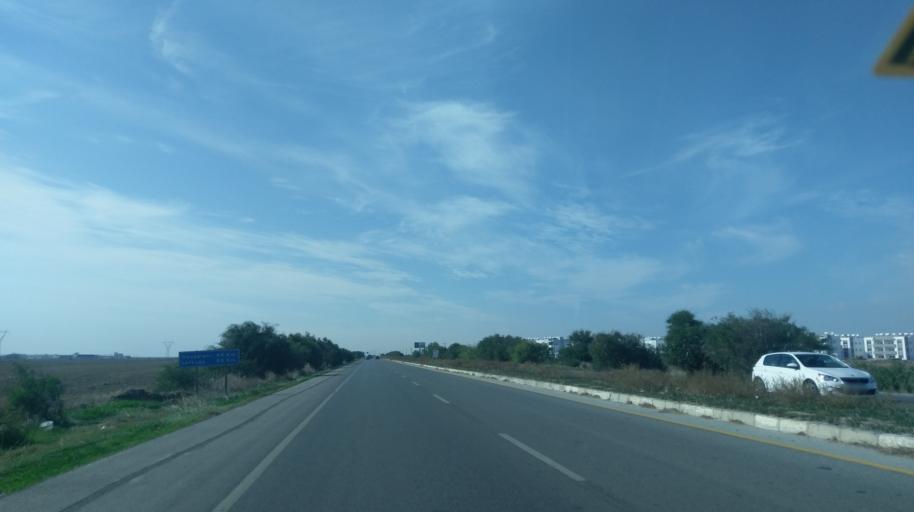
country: CY
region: Ammochostos
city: Acheritou
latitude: 35.1370
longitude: 33.8855
